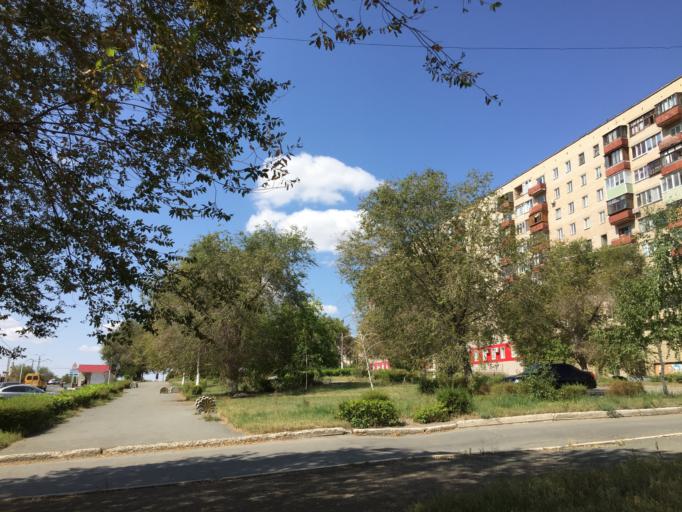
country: RU
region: Orenburg
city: Novotroitsk
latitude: 51.1909
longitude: 58.2739
